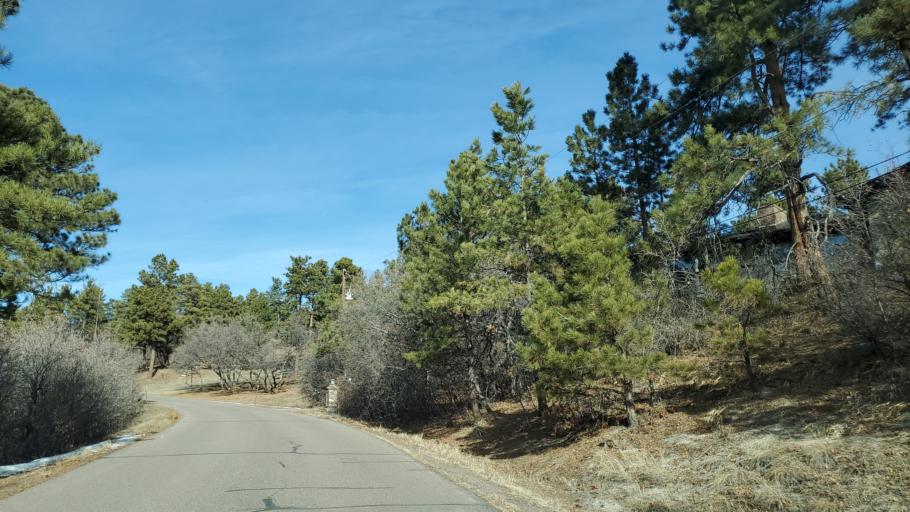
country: US
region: Colorado
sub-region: Douglas County
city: Castle Pines
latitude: 39.4282
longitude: -104.8734
